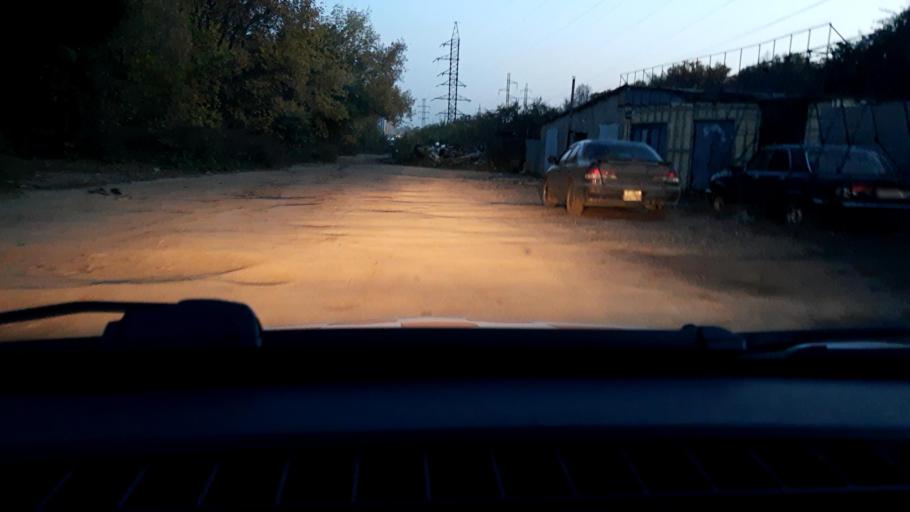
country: RU
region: Bashkortostan
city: Ufa
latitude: 54.8059
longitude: 56.0553
